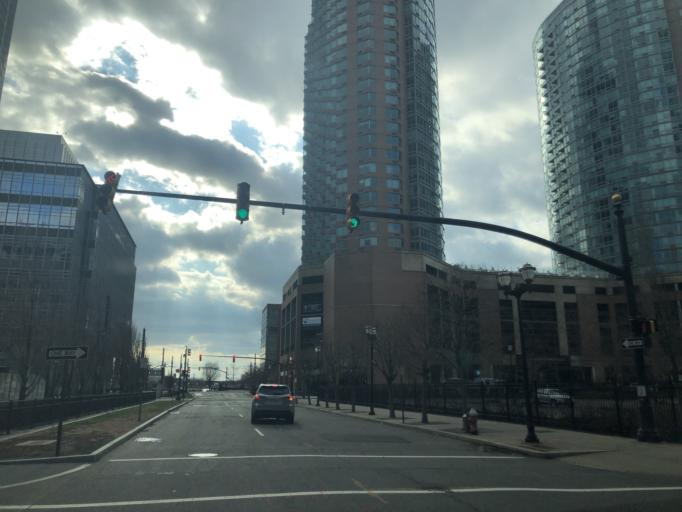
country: US
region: New York
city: New York City
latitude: 40.7142
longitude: -74.0346
